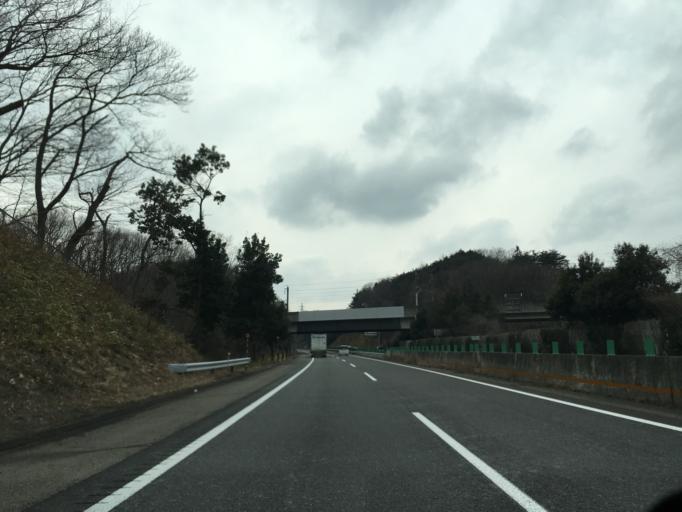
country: JP
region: Fukushima
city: Sukagawa
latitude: 37.1484
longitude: 140.2145
